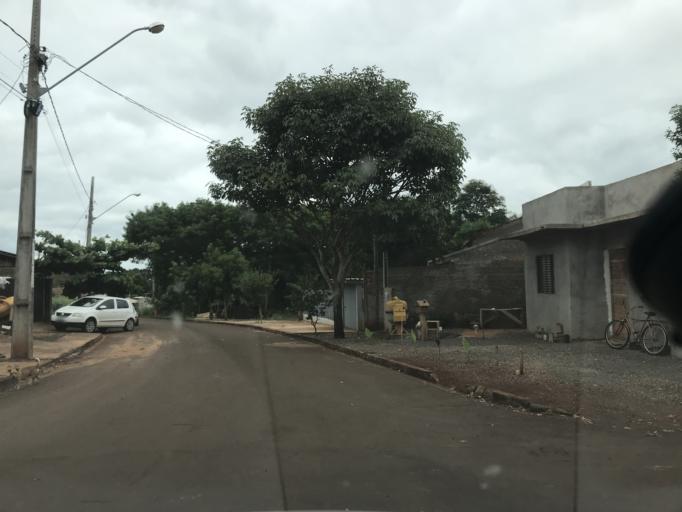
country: BR
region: Parana
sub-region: Palotina
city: Palotina
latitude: -24.3000
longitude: -53.8290
